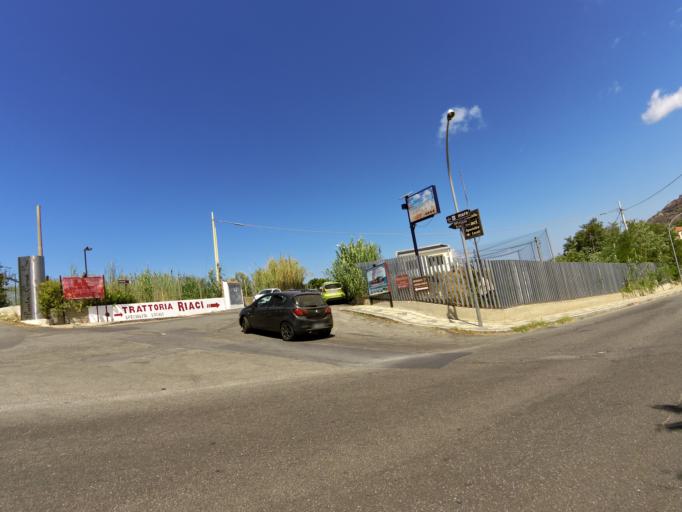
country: IT
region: Calabria
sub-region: Provincia di Vibo-Valentia
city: Santa Domenica
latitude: 38.6670
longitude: 15.8727
